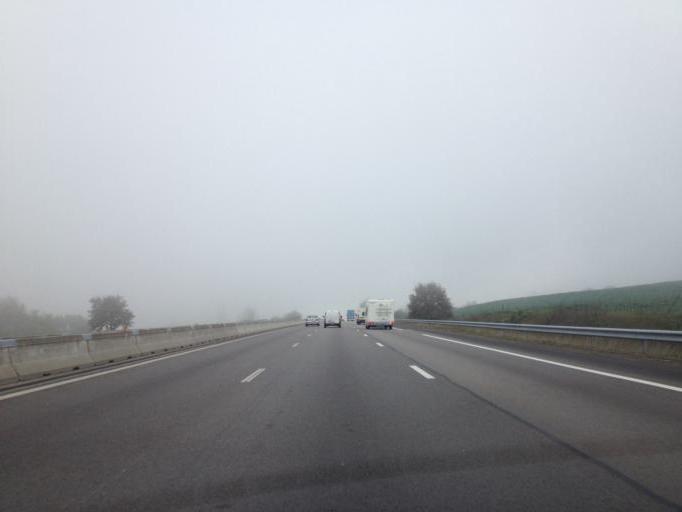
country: FR
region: Rhone-Alpes
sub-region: Departement de la Drome
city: Savasse
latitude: 44.6151
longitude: 4.7930
